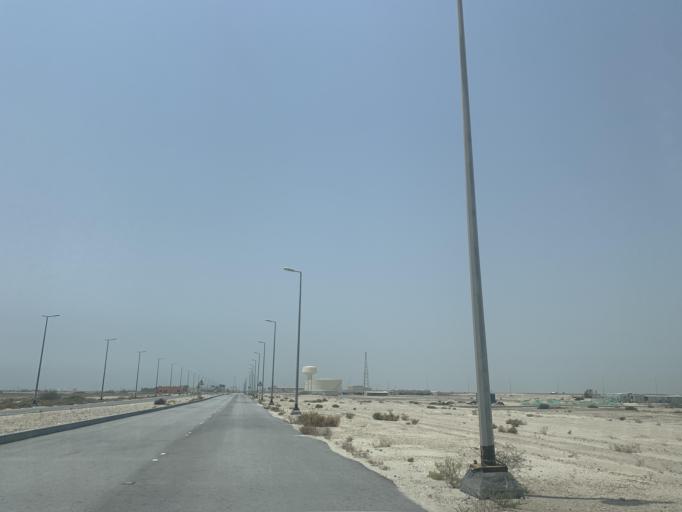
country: BH
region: Central Governorate
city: Dar Kulayb
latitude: 25.8452
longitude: 50.5901
